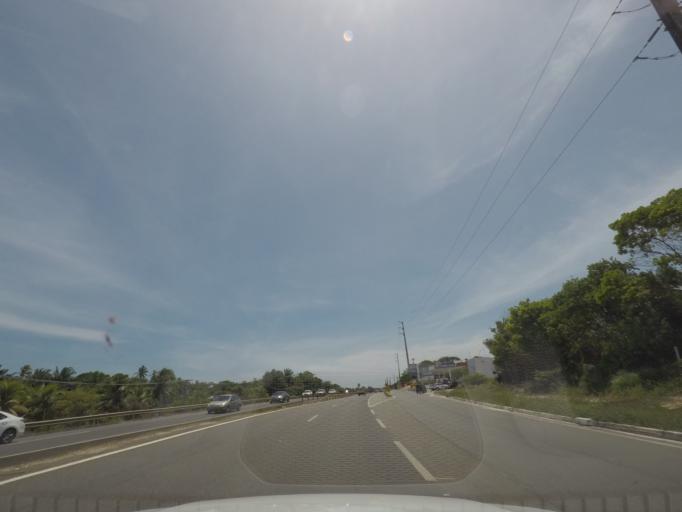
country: BR
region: Bahia
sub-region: Camacari
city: Camacari
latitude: -12.6954
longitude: -38.1261
